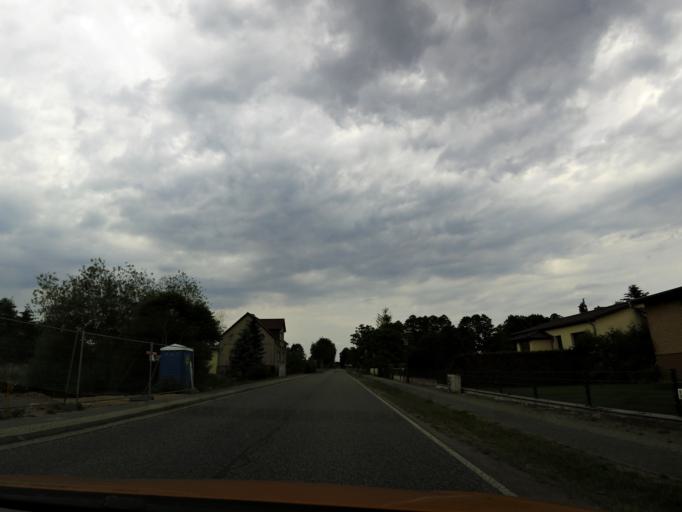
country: DE
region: Brandenburg
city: Baruth
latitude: 52.0543
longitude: 13.5061
